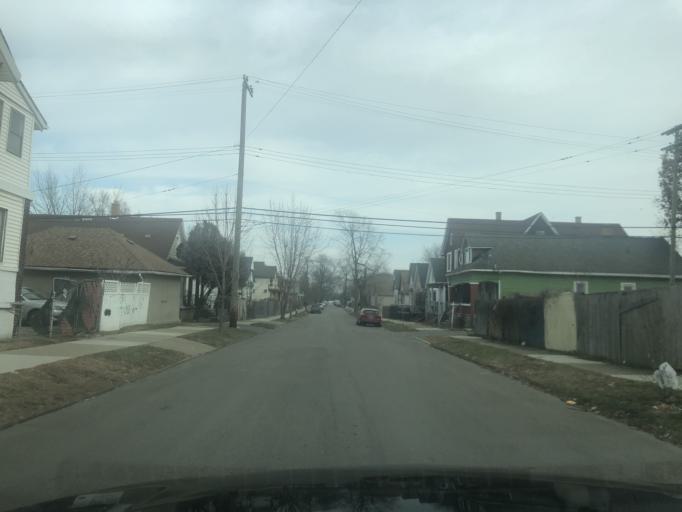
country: US
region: Michigan
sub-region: Wayne County
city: River Rouge
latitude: 42.3218
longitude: -83.1045
